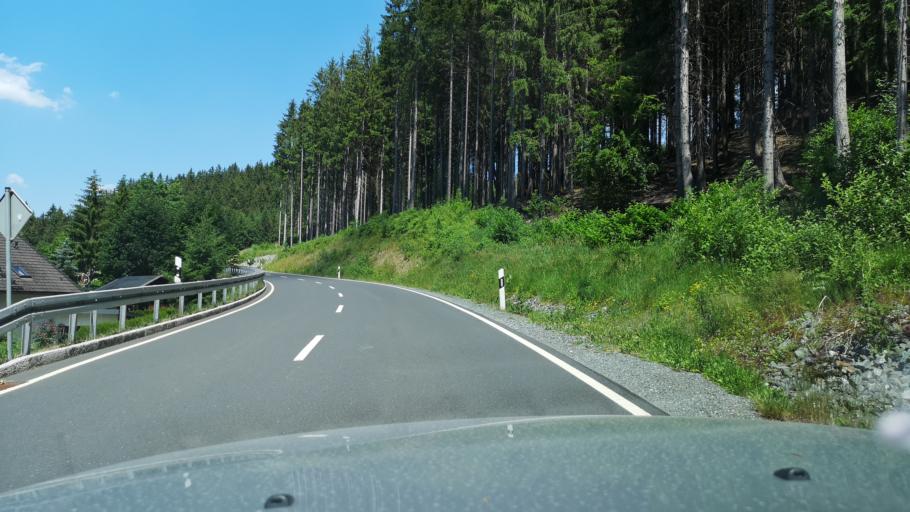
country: DE
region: Bavaria
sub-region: Upper Franconia
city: Teuschnitz
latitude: 50.3913
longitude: 11.3549
